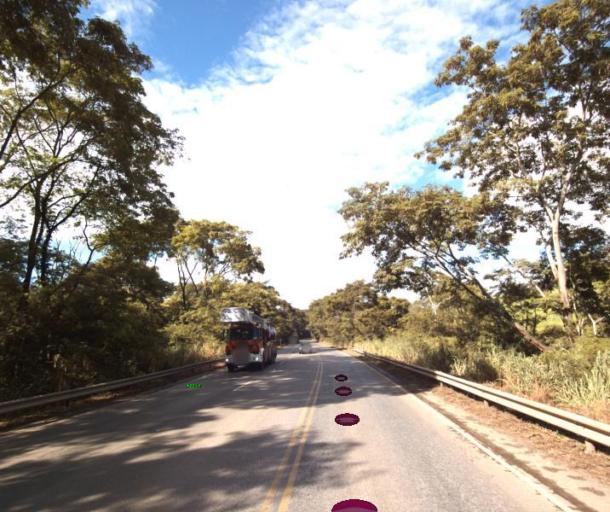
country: BR
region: Goias
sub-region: Uruacu
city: Uruacu
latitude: -14.7197
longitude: -49.2311
